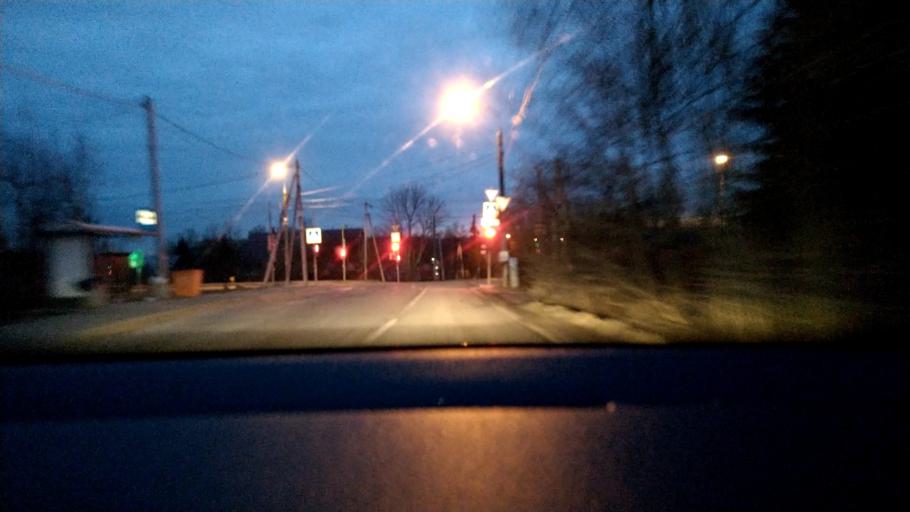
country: RU
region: Moskovskaya
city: Kokoshkino
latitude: 55.6049
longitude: 37.1920
